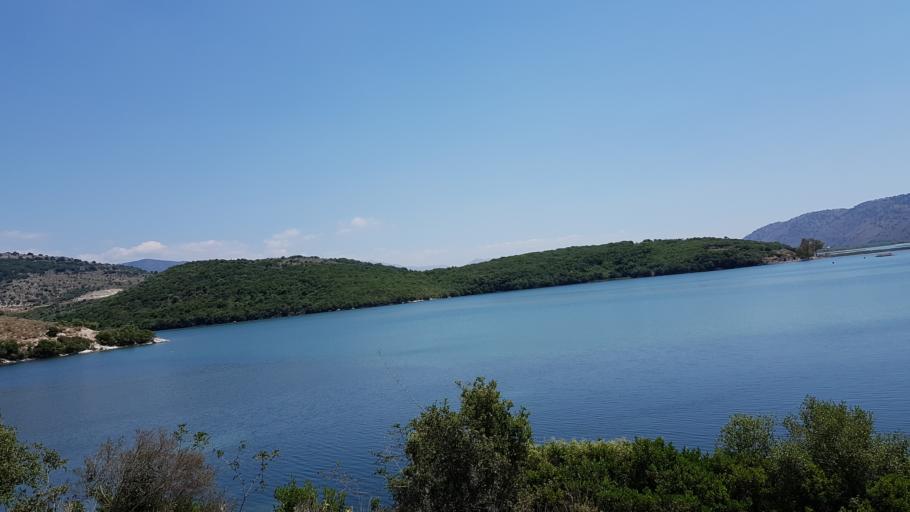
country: AL
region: Vlore
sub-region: Rrethi i Sarandes
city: Xarre
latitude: 39.7494
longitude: 19.9901
